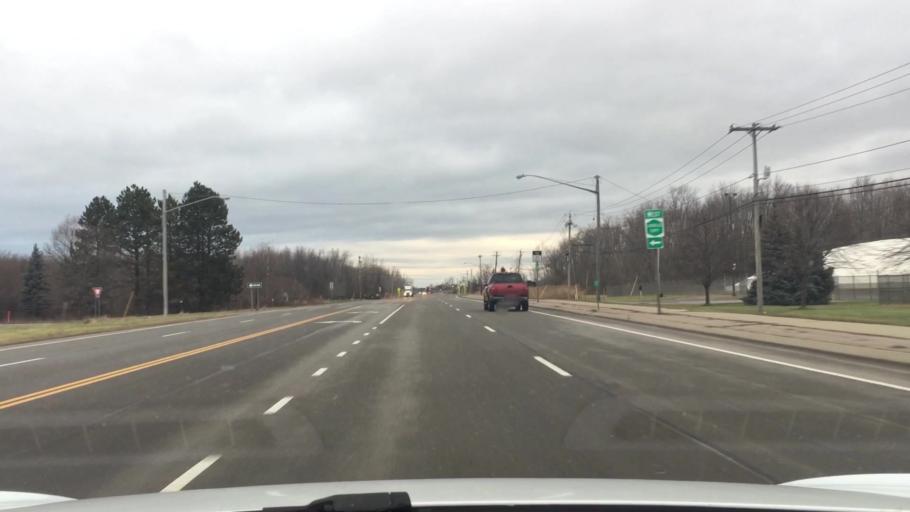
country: US
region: New York
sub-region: Erie County
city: Grandyle Village
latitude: 43.0741
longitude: -78.9405
